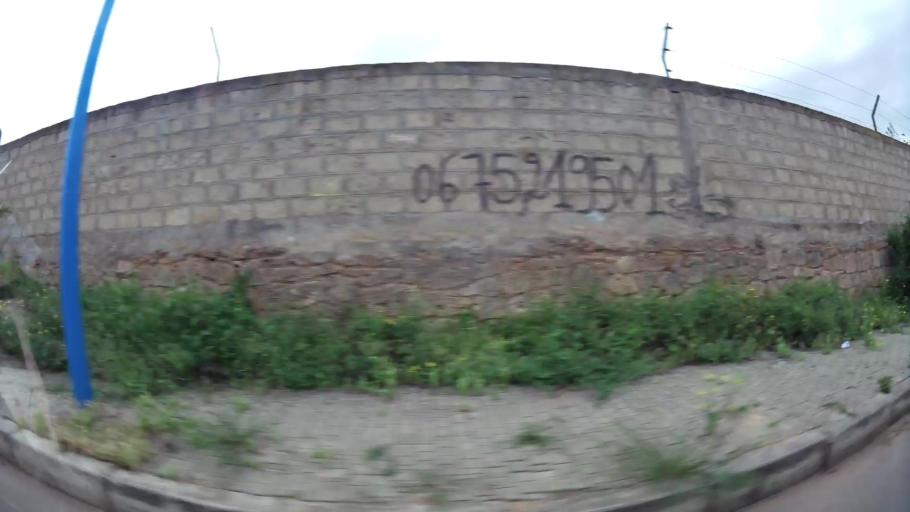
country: MA
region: Grand Casablanca
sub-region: Casablanca
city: Casablanca
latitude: 33.5353
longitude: -7.6359
